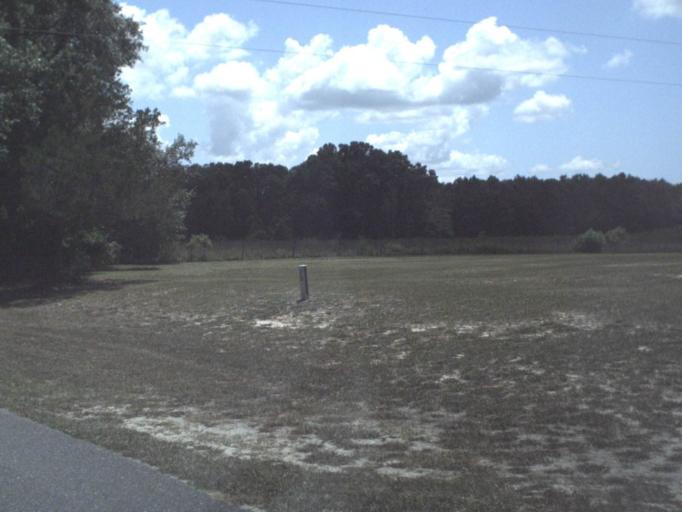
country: US
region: Florida
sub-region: Alachua County
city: High Springs
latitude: 29.7953
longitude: -82.7411
